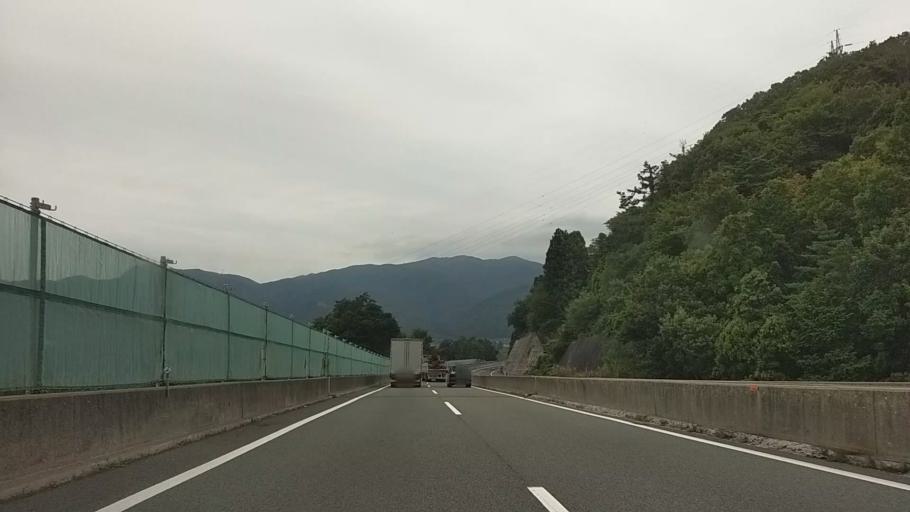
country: JP
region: Nagano
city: Nagano-shi
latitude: 36.5322
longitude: 138.0869
